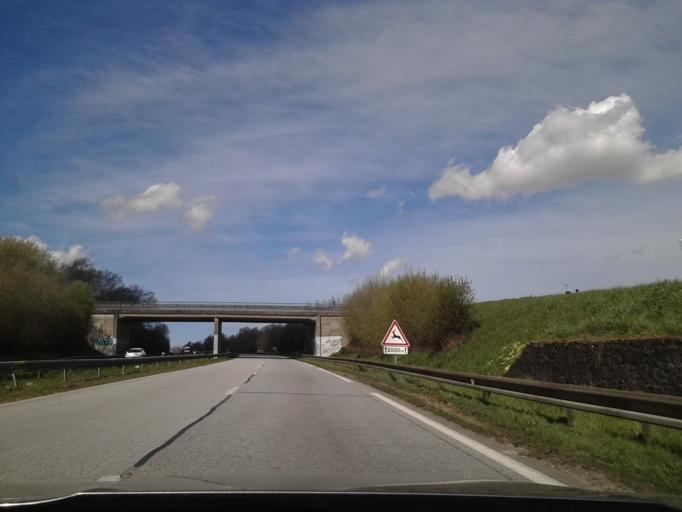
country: FR
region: Lower Normandy
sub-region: Departement de la Manche
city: Brix
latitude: 49.5633
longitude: -1.5683
